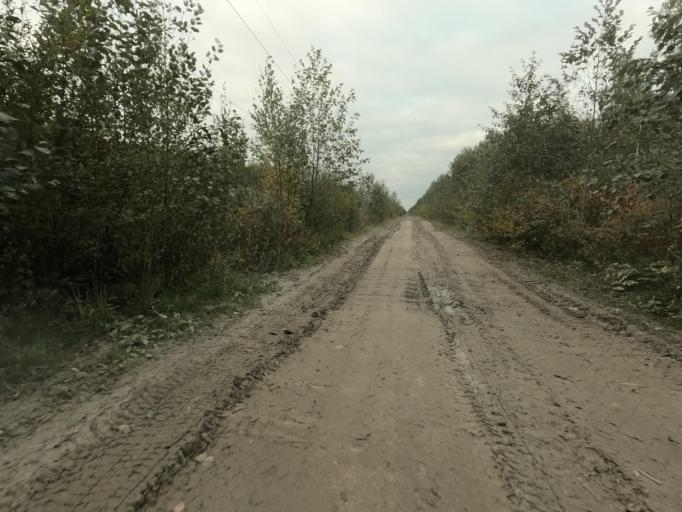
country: RU
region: St.-Petersburg
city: Sapernyy
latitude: 59.7550
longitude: 30.6904
